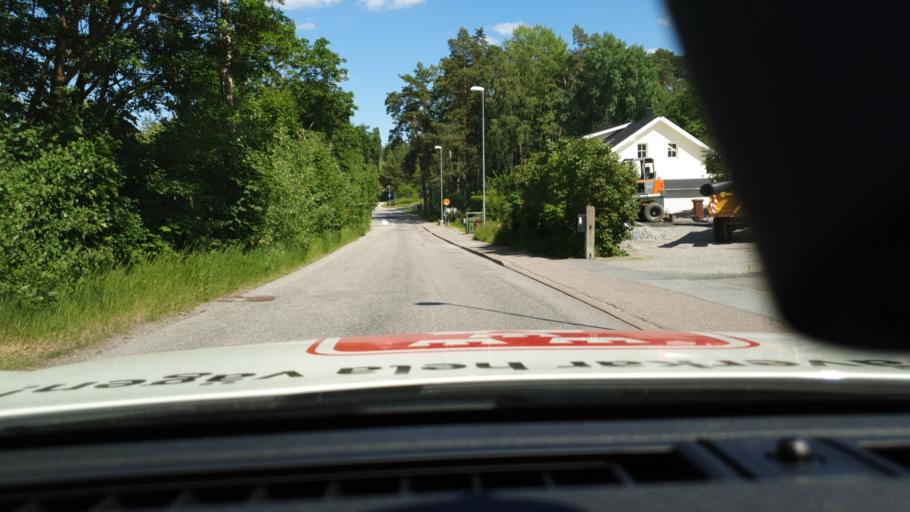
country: SE
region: Stockholm
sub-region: Vallentuna Kommun
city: Vallentuna
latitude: 59.5291
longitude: 18.0876
